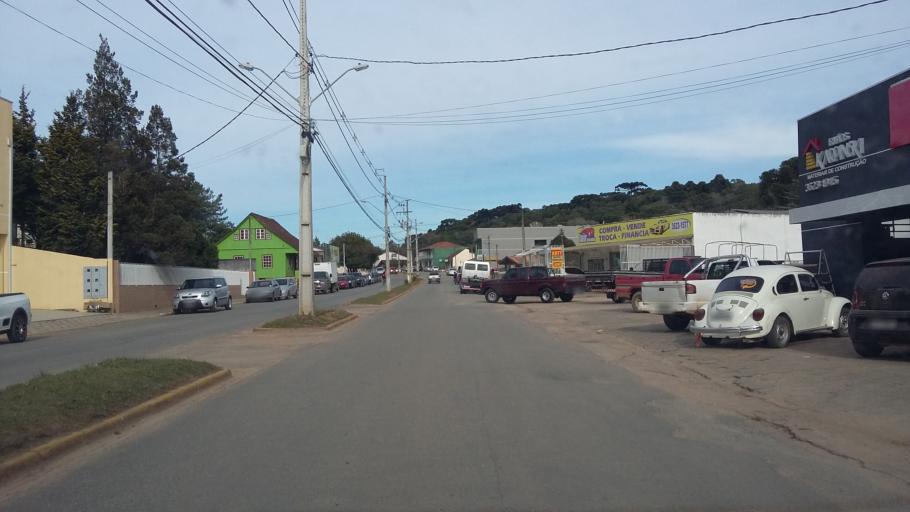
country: BR
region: Parana
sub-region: Lapa
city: Lapa
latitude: -25.8738
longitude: -49.4999
